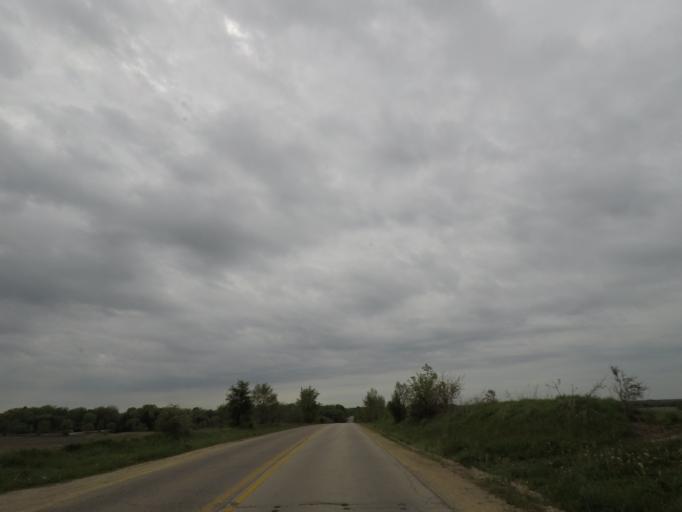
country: US
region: Illinois
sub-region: Winnebago County
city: Roscoe
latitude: 42.4456
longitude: -88.9883
